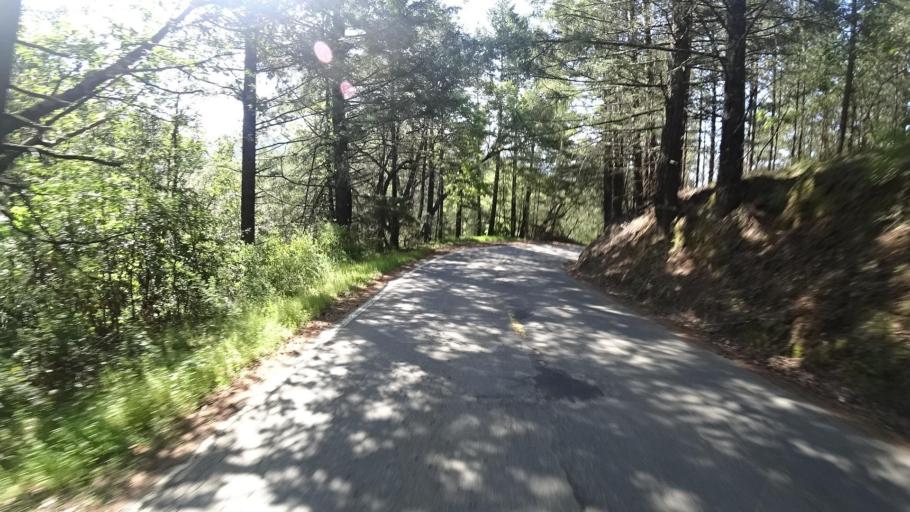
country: US
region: California
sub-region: Humboldt County
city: Redway
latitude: 40.1108
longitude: -123.7663
